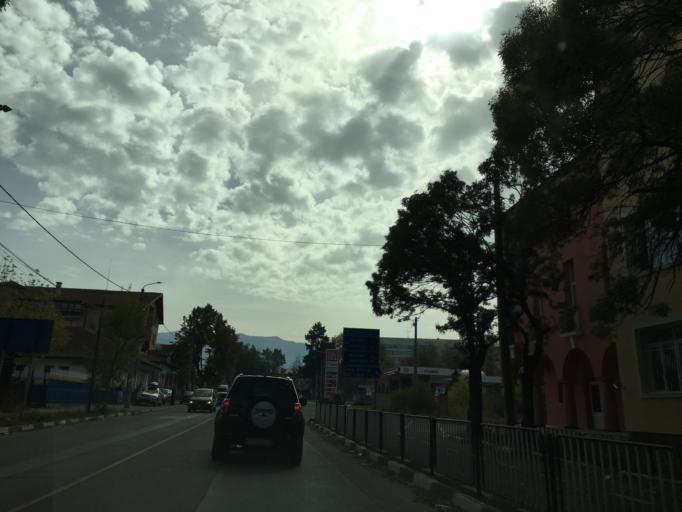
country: BG
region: Sofiya
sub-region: Obshtina Samokov
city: Samokov
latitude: 42.3383
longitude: 23.5526
